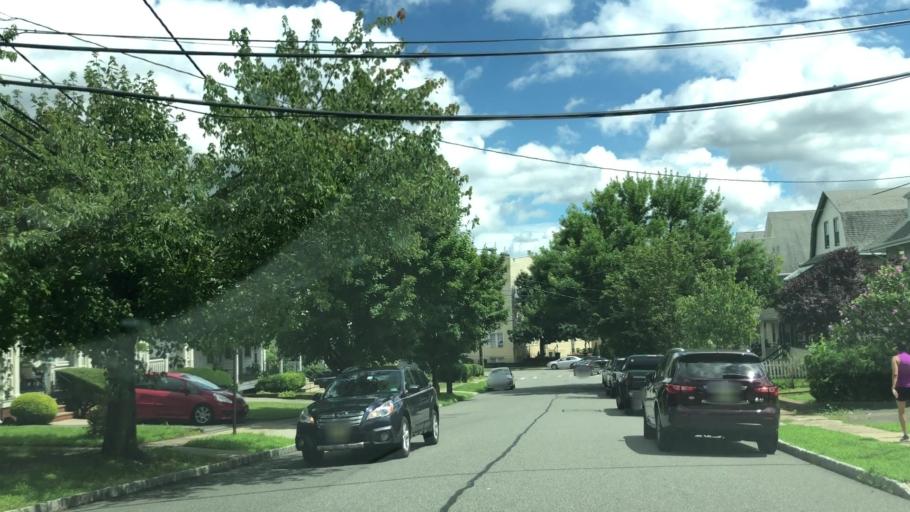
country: US
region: New Jersey
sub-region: Essex County
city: Glen Ridge
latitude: 40.8078
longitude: -74.2167
